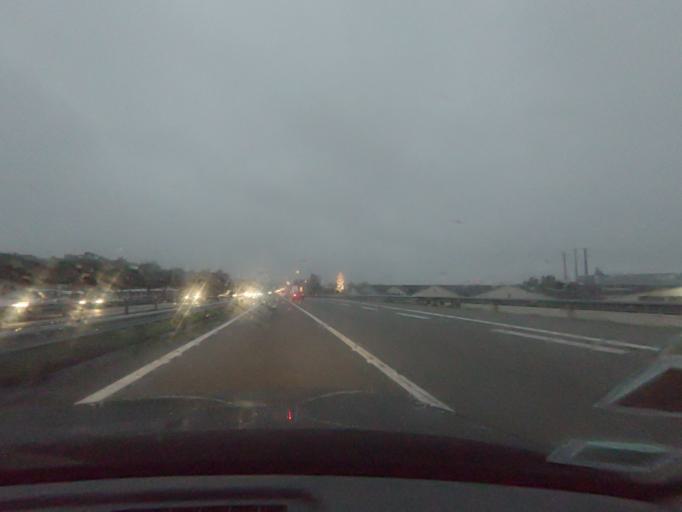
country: PT
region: Porto
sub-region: Matosinhos
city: Santa Cruz do Bispo
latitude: 41.2366
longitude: -8.6961
